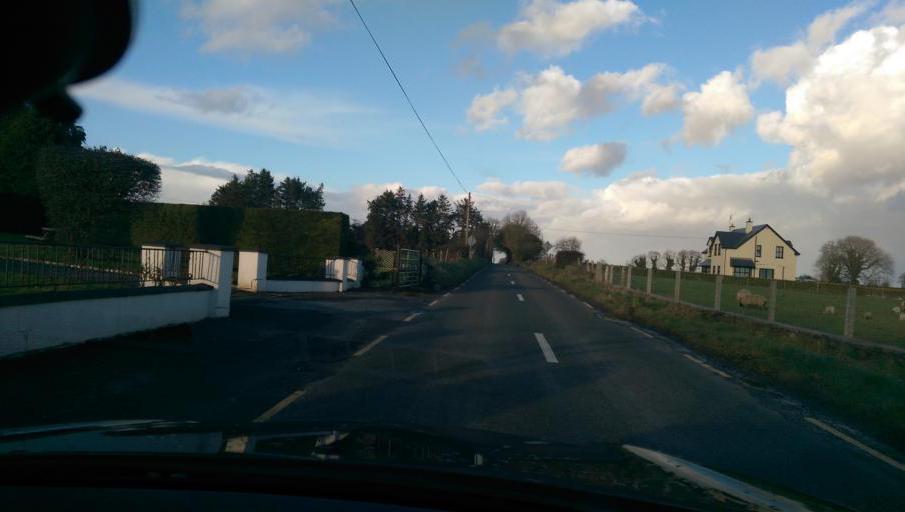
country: IE
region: Connaught
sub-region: County Galway
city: Loughrea
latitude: 53.3936
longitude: -8.4801
